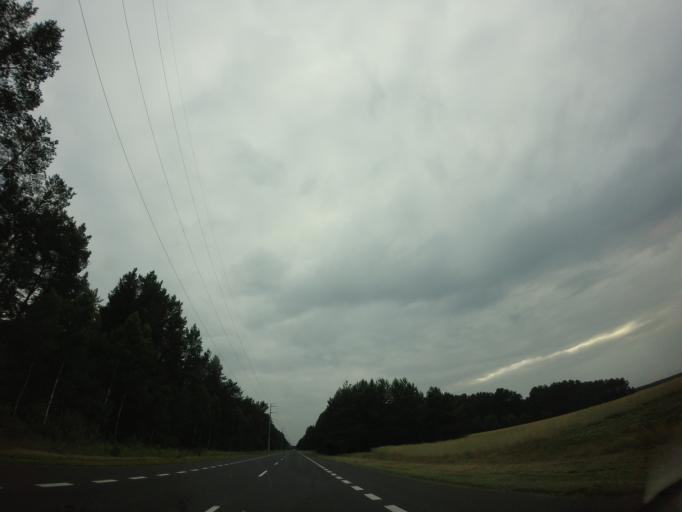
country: PL
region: West Pomeranian Voivodeship
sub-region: Powiat walecki
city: Miroslawiec
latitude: 53.3882
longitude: 16.1608
